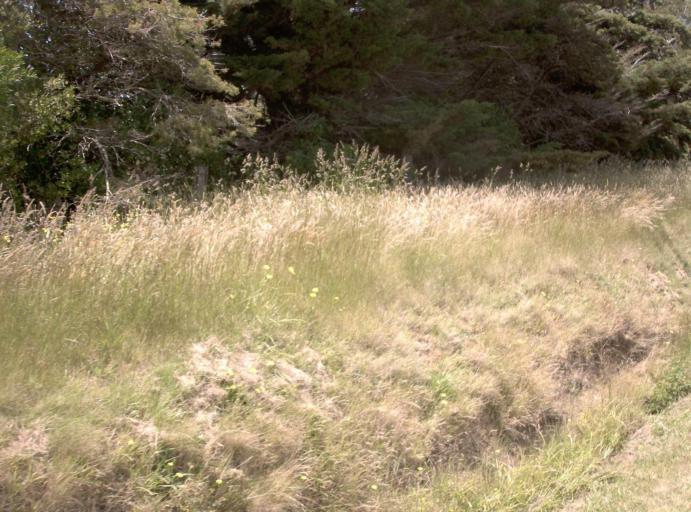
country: AU
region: Victoria
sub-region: Bass Coast
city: North Wonthaggi
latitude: -38.7168
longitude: 146.1033
